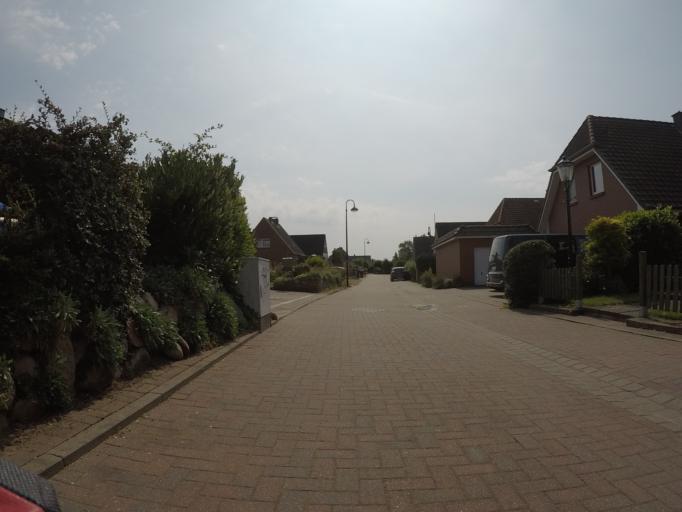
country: DE
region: Schleswig-Holstein
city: Kisdorf
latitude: 53.8067
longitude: 10.0107
